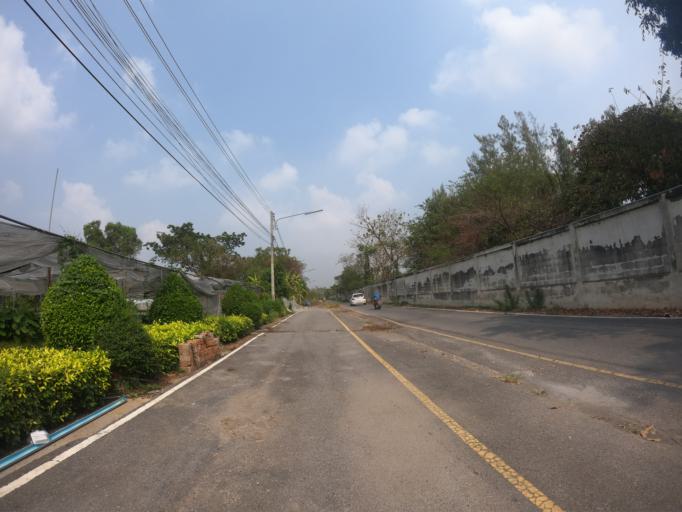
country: TH
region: Pathum Thani
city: Nong Suea
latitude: 14.0633
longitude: 100.8501
